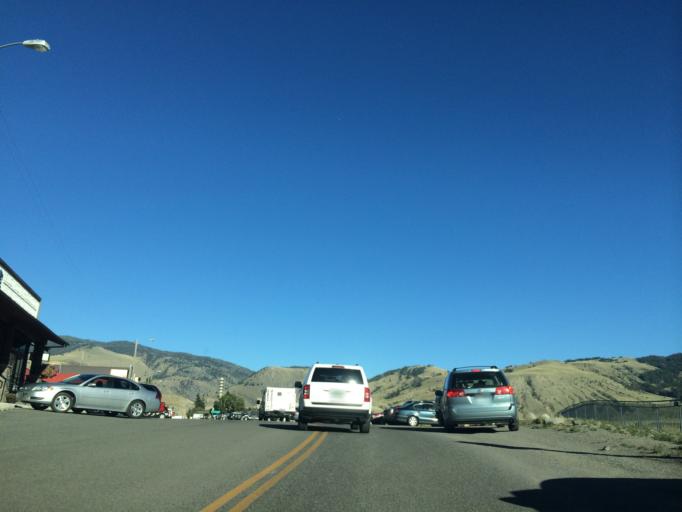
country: US
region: Montana
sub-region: Gallatin County
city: West Yellowstone
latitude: 45.0297
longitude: -110.7083
